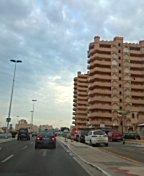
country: ES
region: Murcia
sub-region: Murcia
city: La Manga del Mar Menor
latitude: 37.6785
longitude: -0.7335
